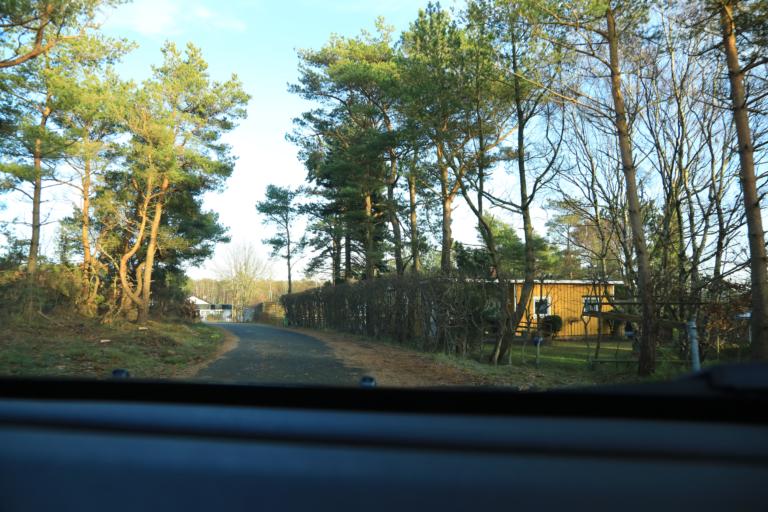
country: SE
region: Halland
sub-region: Varbergs Kommun
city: Varberg
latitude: 57.1914
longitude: 12.1689
